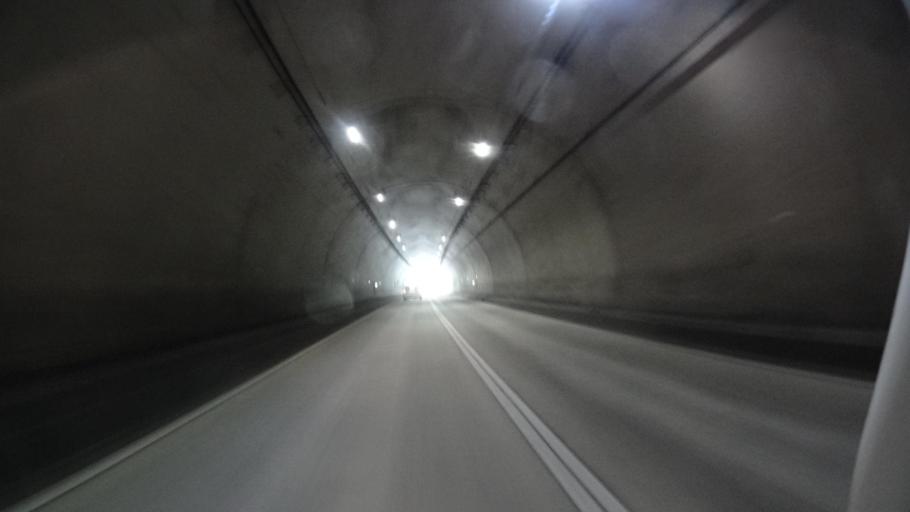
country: JP
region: Kyoto
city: Kameoka
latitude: 35.2225
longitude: 135.5720
